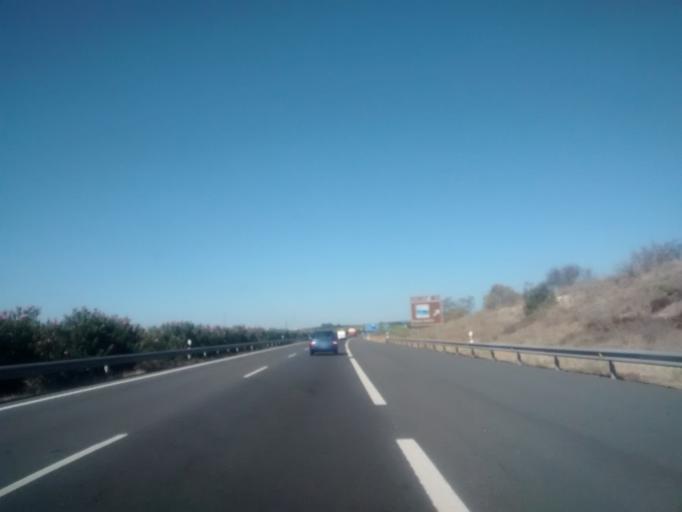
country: ES
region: Andalusia
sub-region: Provincia de Huelva
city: Aljaraque
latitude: 37.3249
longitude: -7.0571
